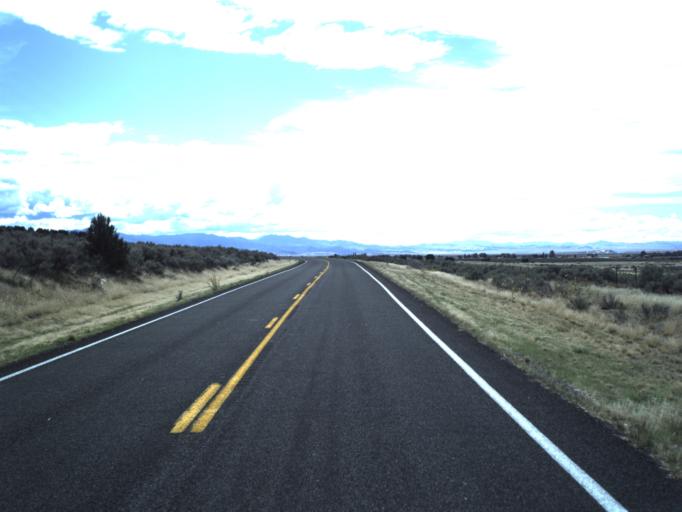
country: US
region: Utah
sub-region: Millard County
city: Fillmore
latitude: 39.0043
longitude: -112.4116
